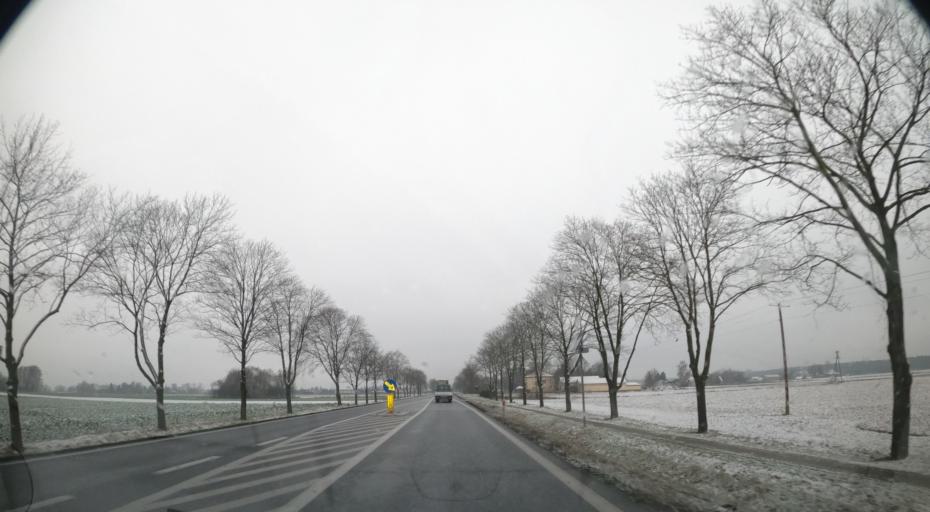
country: PL
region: Masovian Voivodeship
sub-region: Powiat sochaczewski
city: Paprotnia
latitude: 52.2096
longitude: 20.4554
